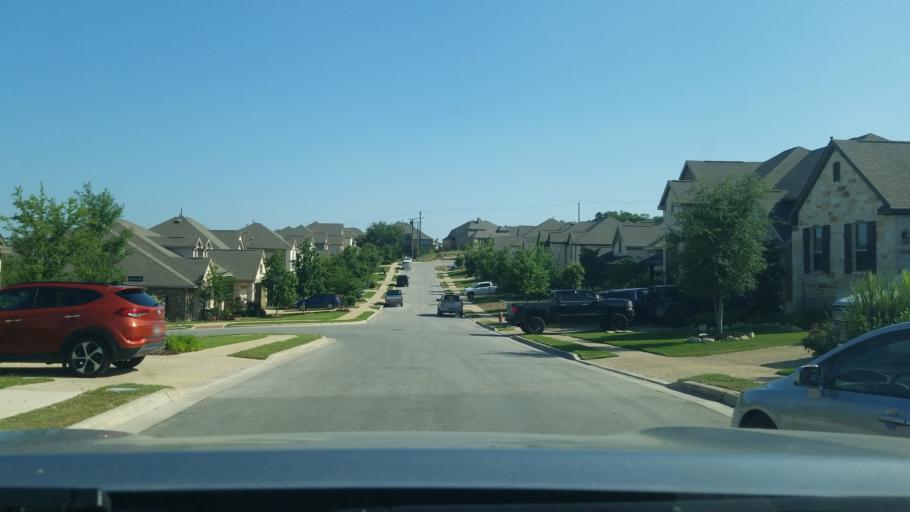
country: US
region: Texas
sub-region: Comal County
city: Bulverde
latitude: 29.7743
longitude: -98.4219
